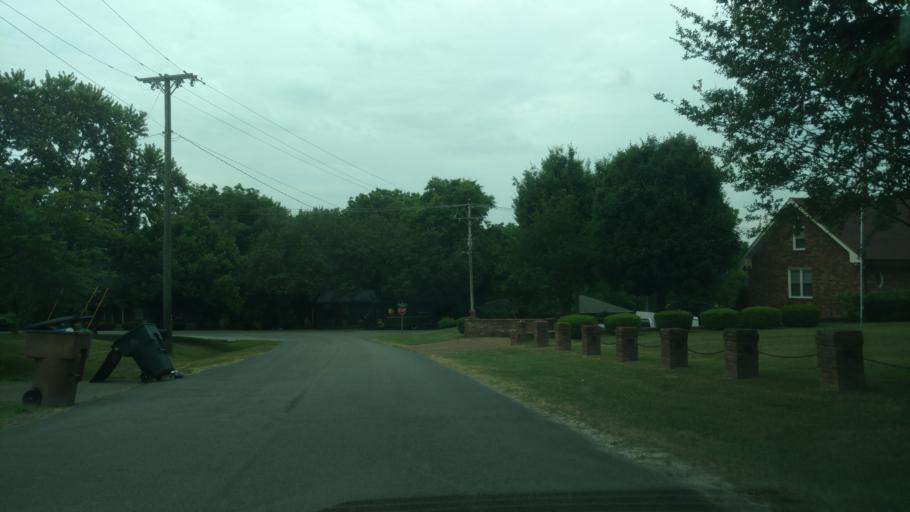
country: US
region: Tennessee
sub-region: Davidson County
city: Nashville
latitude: 36.2001
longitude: -86.7116
